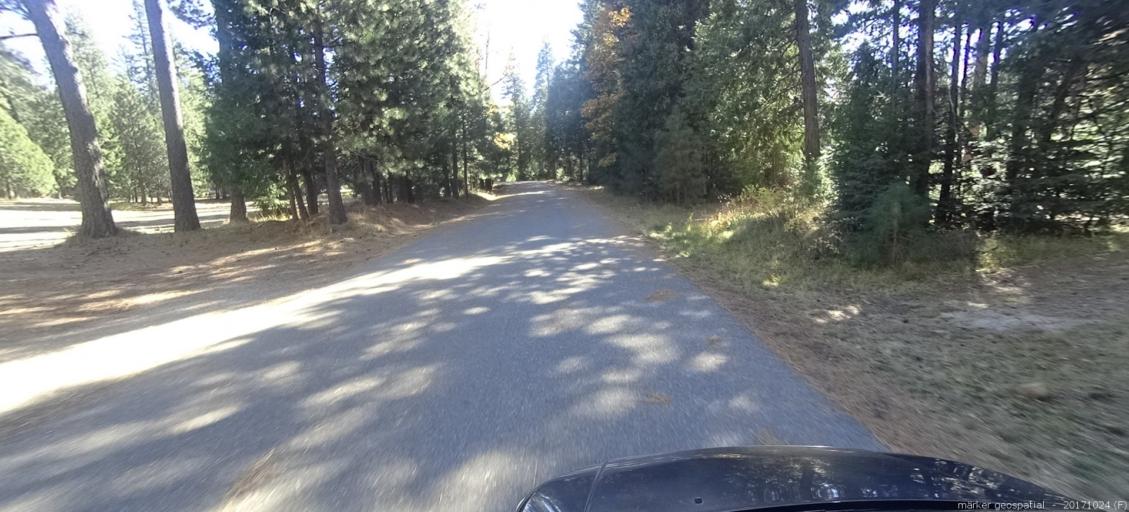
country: US
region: California
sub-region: Shasta County
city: Shingletown
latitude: 40.5179
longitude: -121.6819
